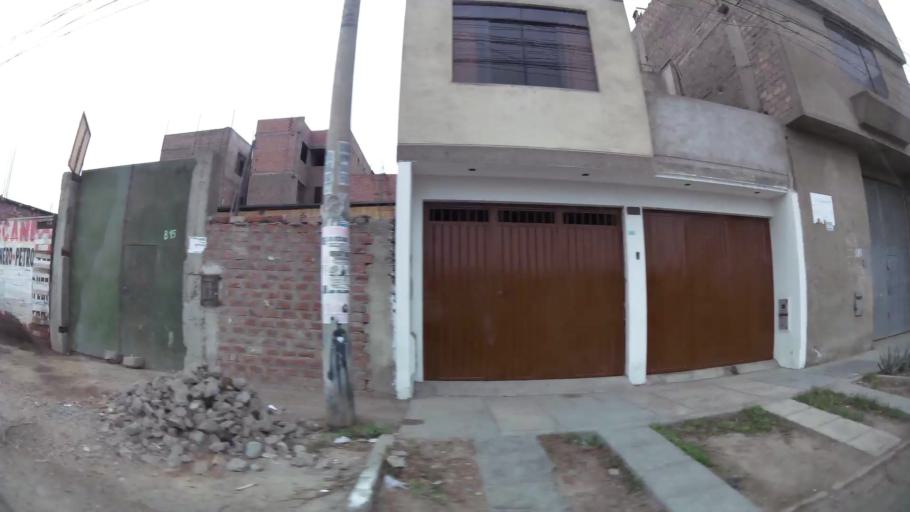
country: PE
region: Lima
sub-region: Lima
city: Independencia
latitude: -11.9576
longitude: -77.0596
